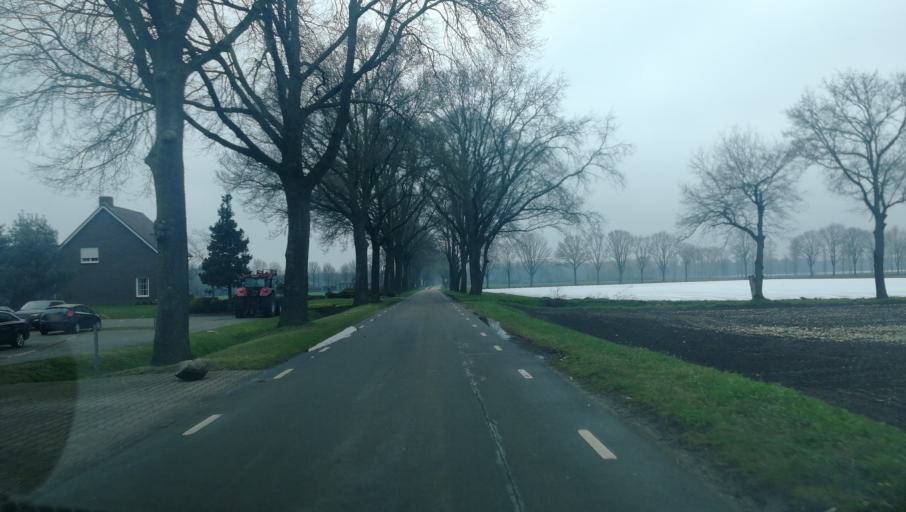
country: NL
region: Limburg
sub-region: Gemeente Beesel
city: Beesel
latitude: 51.2864
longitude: 6.0122
